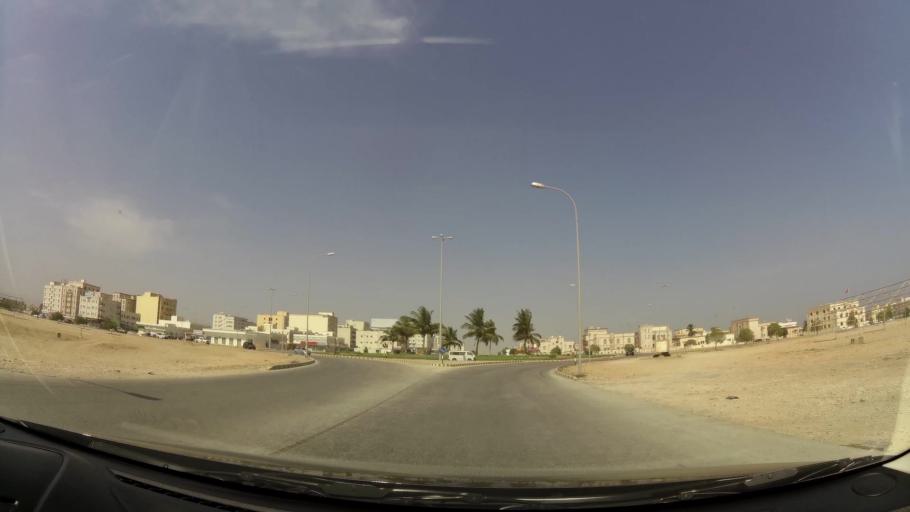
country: OM
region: Zufar
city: Salalah
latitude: 17.0505
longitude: 54.1478
